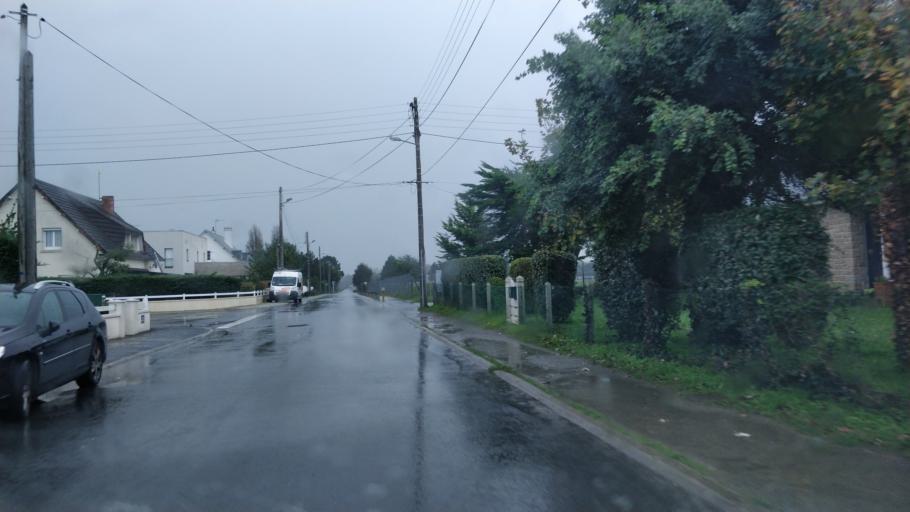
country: FR
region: Lower Normandy
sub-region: Departement de la Manche
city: Brehal
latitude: 48.9025
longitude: -1.5651
